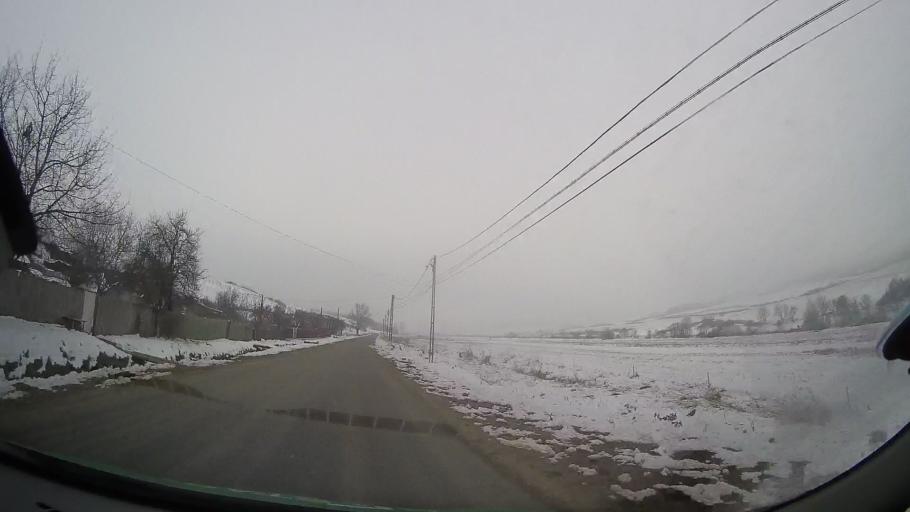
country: RO
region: Bacau
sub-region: Comuna Vultureni
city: Vultureni
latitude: 46.3191
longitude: 27.2928
